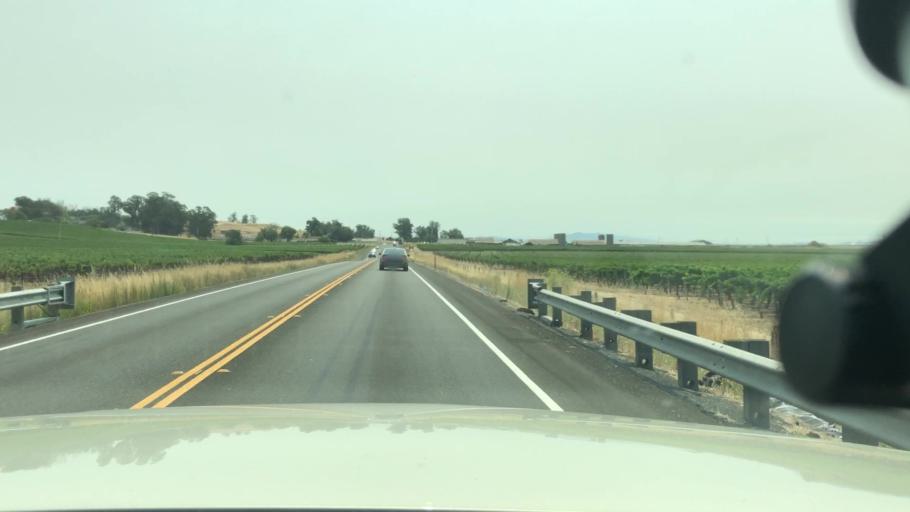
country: US
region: California
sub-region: Marin County
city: Black Point-Green Point
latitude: 38.1621
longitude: -122.5052
